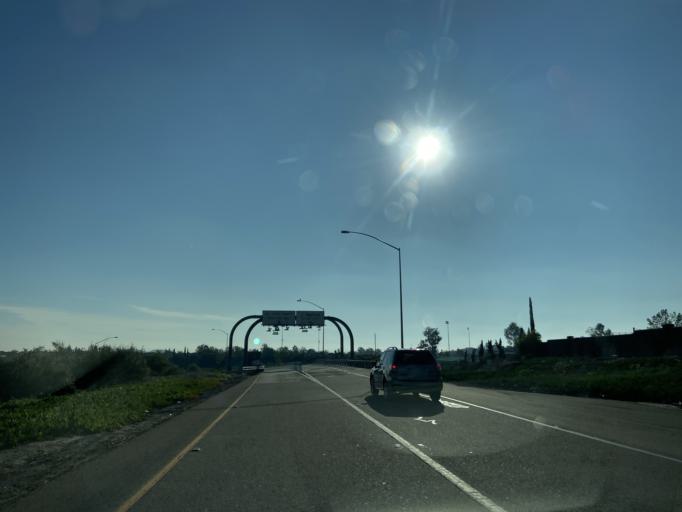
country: US
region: California
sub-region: San Diego County
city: Bonita
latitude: 32.6226
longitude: -116.9723
